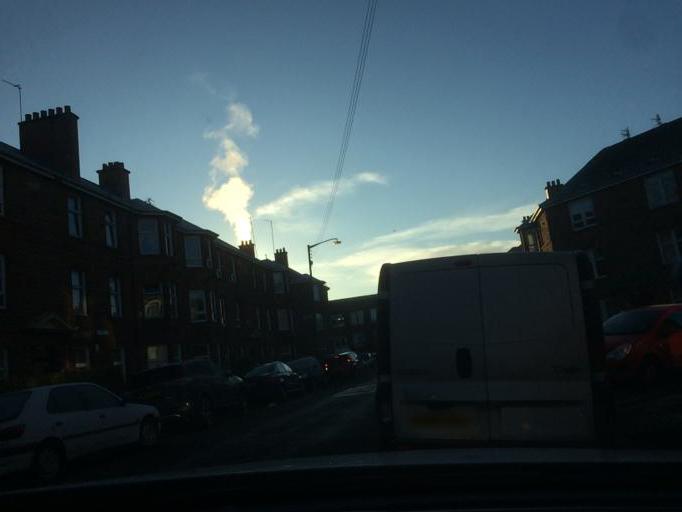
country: GB
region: Scotland
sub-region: East Renfrewshire
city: Giffnock
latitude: 55.8321
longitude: -4.2825
